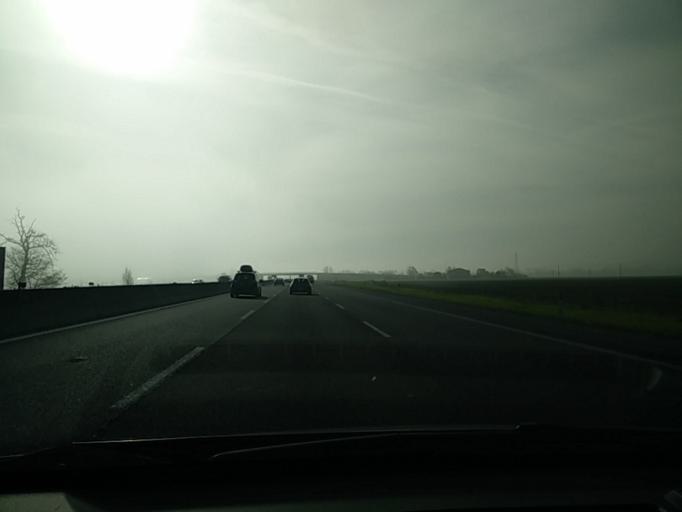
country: IT
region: Emilia-Romagna
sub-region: Provincia di Bologna
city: Osteria Grande
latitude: 44.4522
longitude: 11.5380
